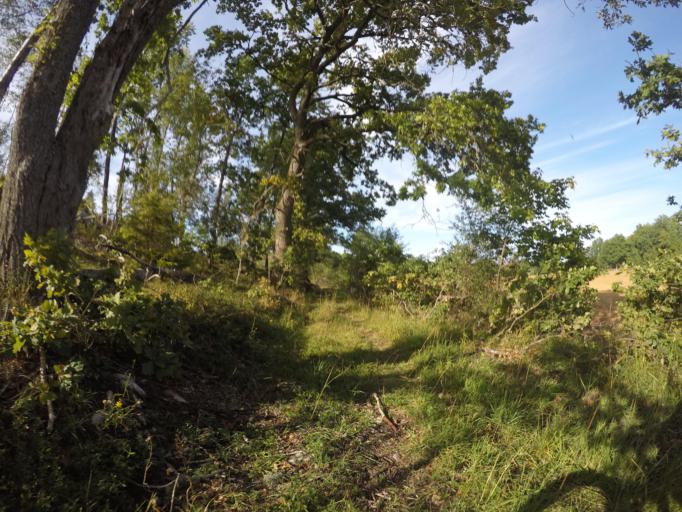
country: SE
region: Soedermanland
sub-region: Eskilstuna Kommun
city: Kvicksund
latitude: 59.5135
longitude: 16.3048
